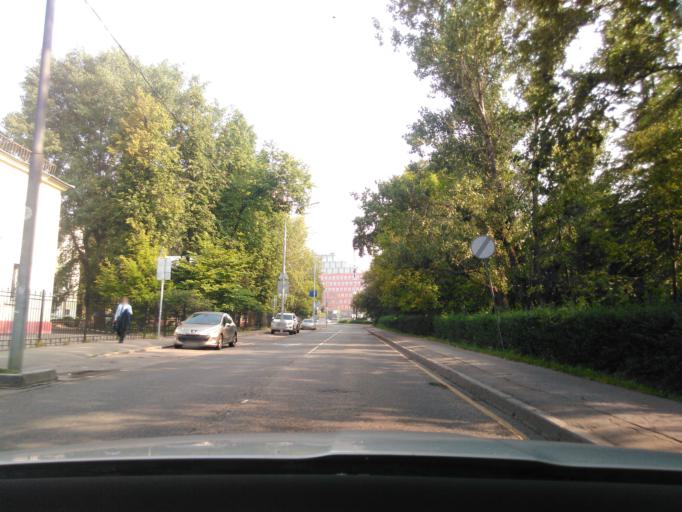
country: RU
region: Moscow
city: Sokol
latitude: 55.8014
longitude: 37.5198
